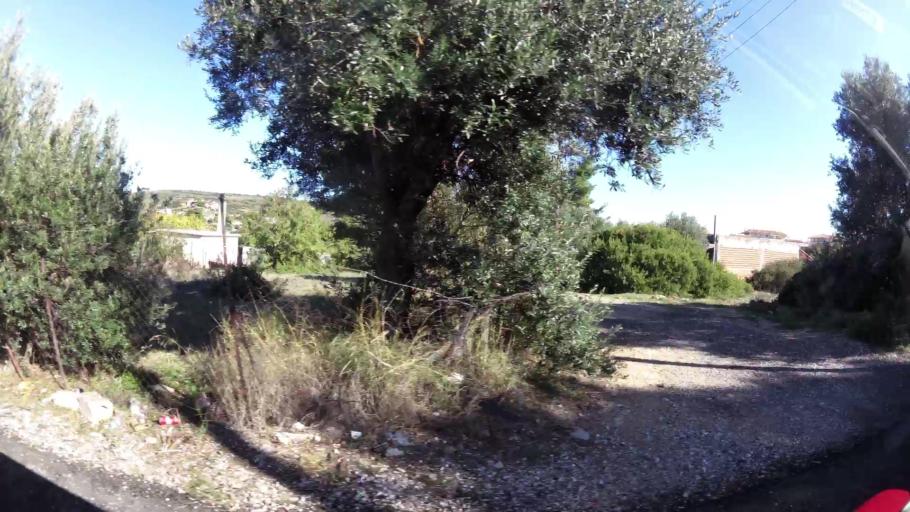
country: GR
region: Attica
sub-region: Nomarchia Anatolikis Attikis
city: Pallini
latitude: 38.0103
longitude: 23.8760
